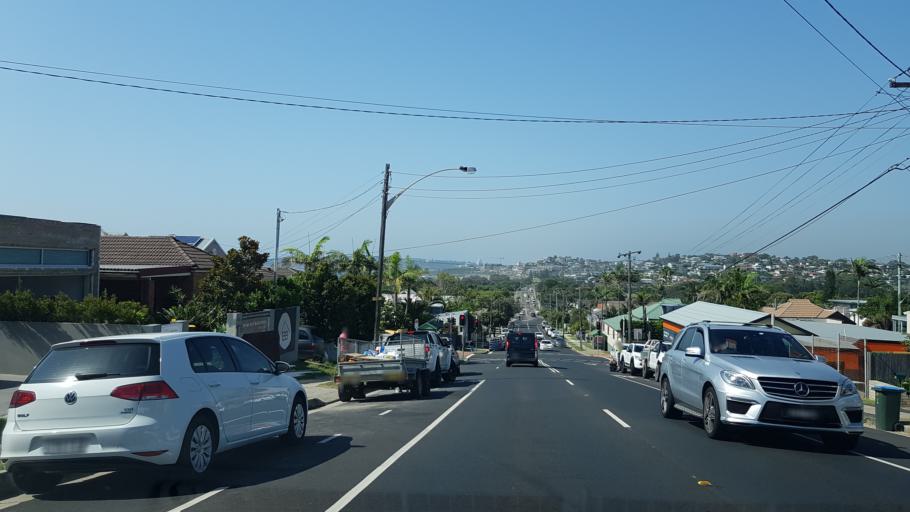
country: AU
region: New South Wales
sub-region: Warringah
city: North Curl Curl
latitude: -33.7619
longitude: 151.2957
